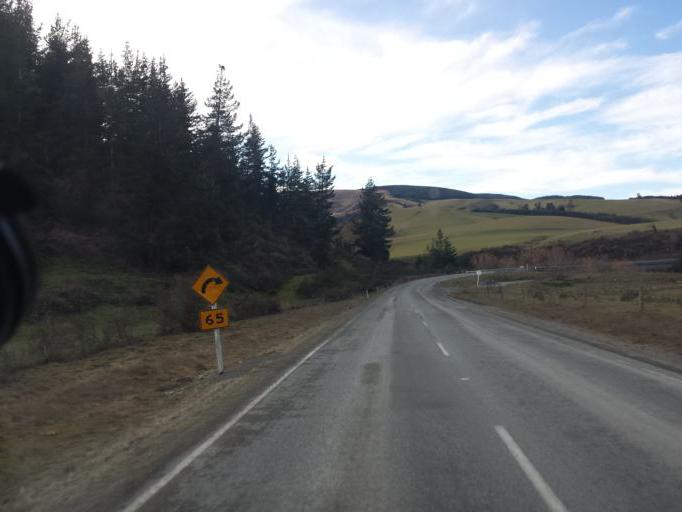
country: NZ
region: Canterbury
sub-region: Timaru District
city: Pleasant Point
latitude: -44.0809
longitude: 170.9760
